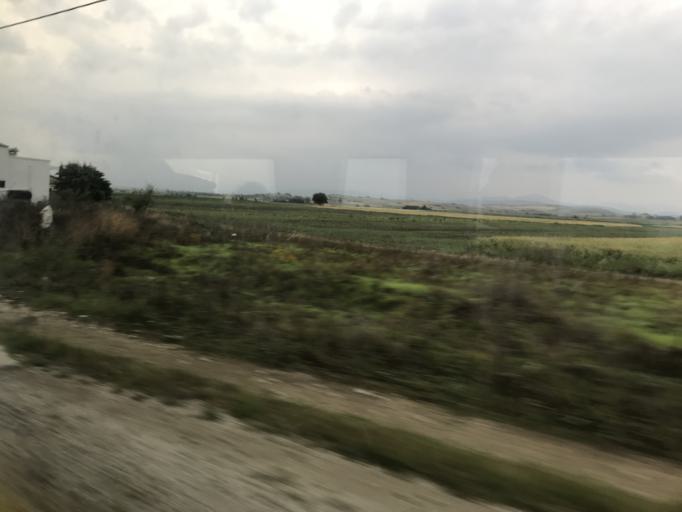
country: GR
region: East Macedonia and Thrace
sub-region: Nomos Rodopis
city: Aratos
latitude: 41.0834
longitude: 25.5431
